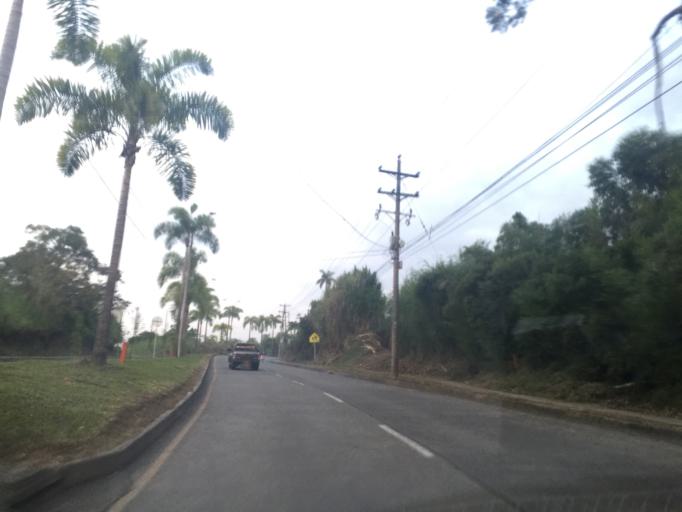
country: CO
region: Risaralda
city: Pereira
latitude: 4.8002
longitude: -75.7544
